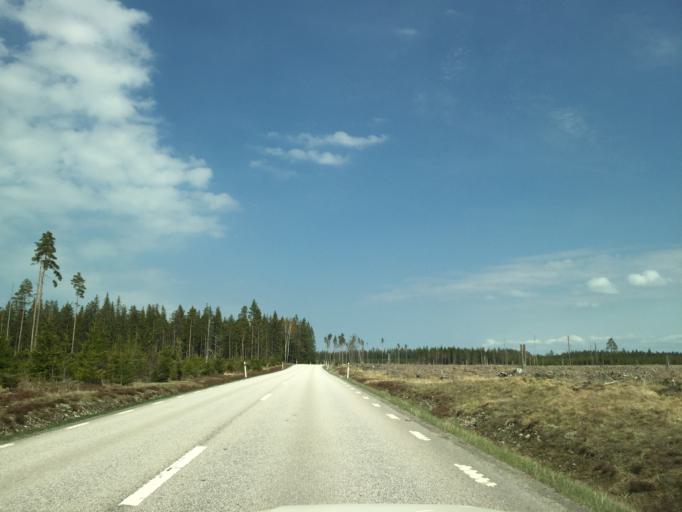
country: SE
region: Vaestra Goetaland
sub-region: Bengtsfors Kommun
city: Dals Langed
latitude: 58.8308
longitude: 12.1426
